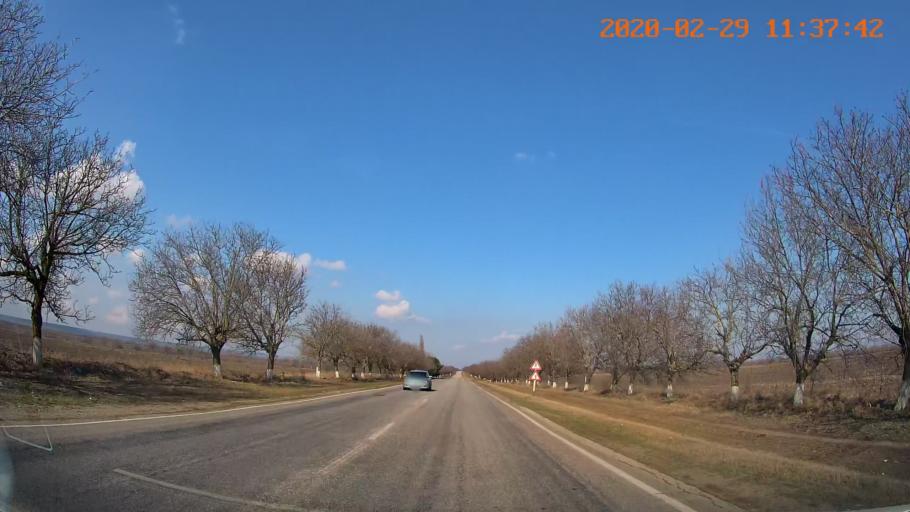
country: MD
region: Rezina
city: Saharna
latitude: 47.6152
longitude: 29.0438
